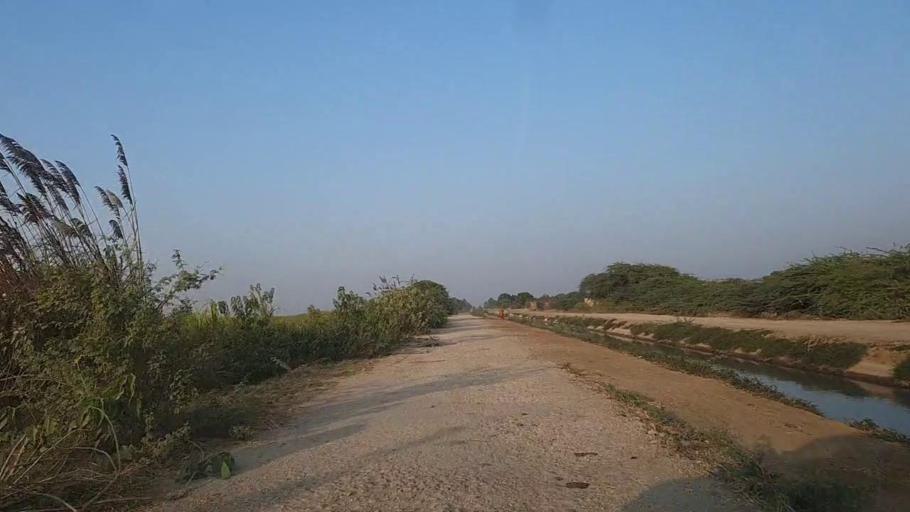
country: PK
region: Sindh
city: Mirpur Sakro
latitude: 24.2893
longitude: 67.6926
